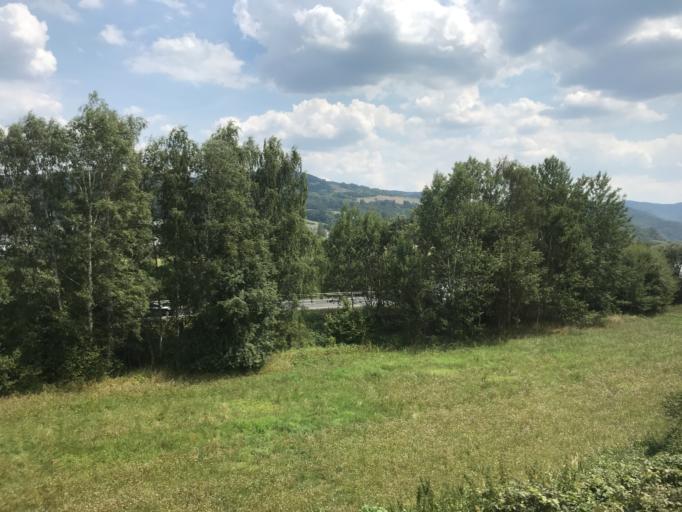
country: CZ
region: Ustecky
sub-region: Okres Decin
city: Decin
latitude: 50.7373
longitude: 14.1796
